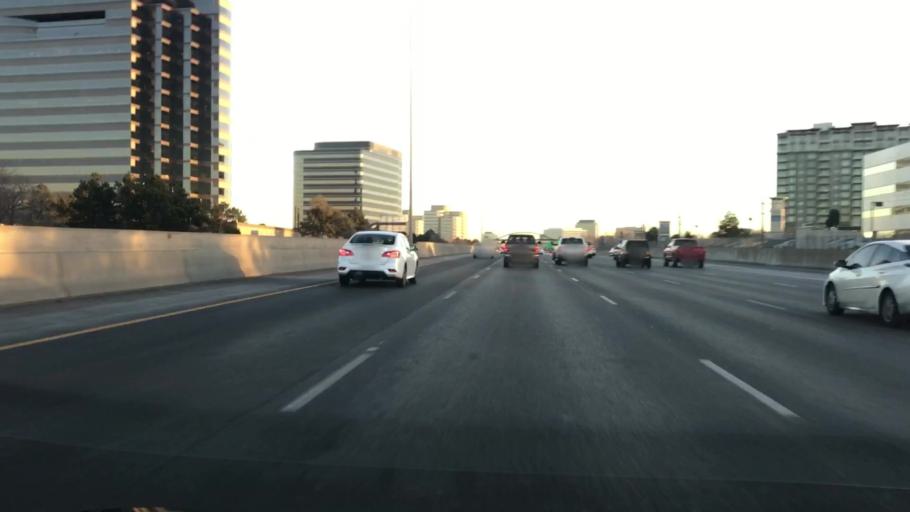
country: US
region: Colorado
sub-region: Arapahoe County
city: Castlewood
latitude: 39.6214
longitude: -104.9015
